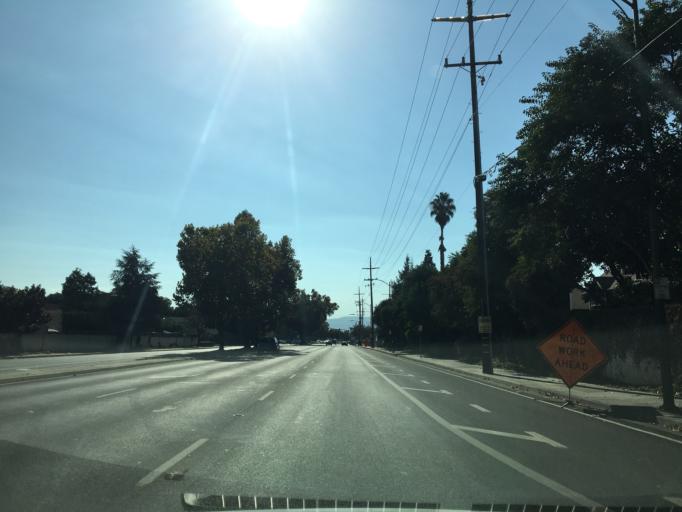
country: US
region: California
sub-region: Santa Clara County
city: San Jose
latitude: 37.3760
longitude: -121.8711
